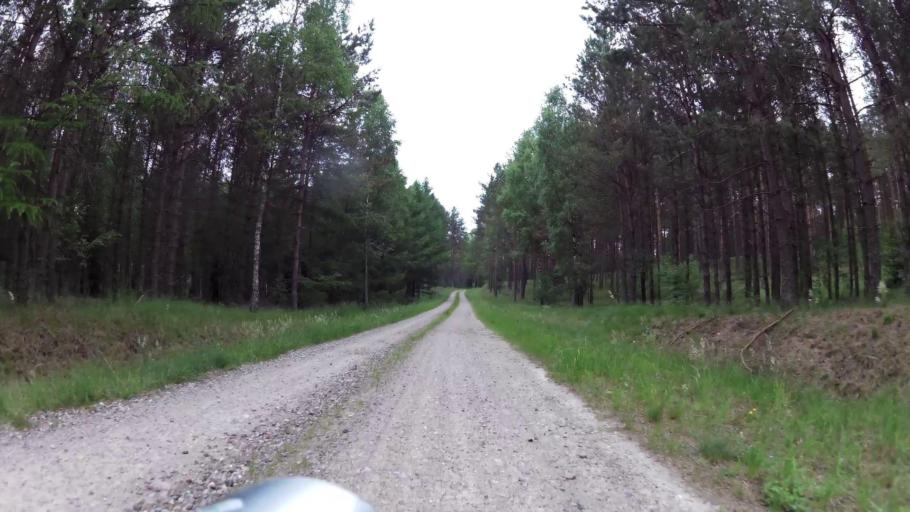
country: PL
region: West Pomeranian Voivodeship
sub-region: Powiat szczecinecki
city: Bialy Bor
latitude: 53.9522
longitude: 16.8338
